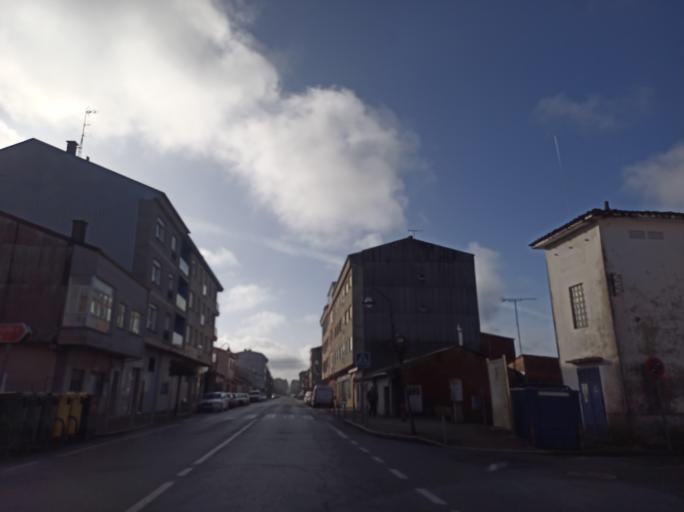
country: ES
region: Galicia
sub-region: Provincia da Coruna
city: Curtis
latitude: 43.1379
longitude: -8.0360
